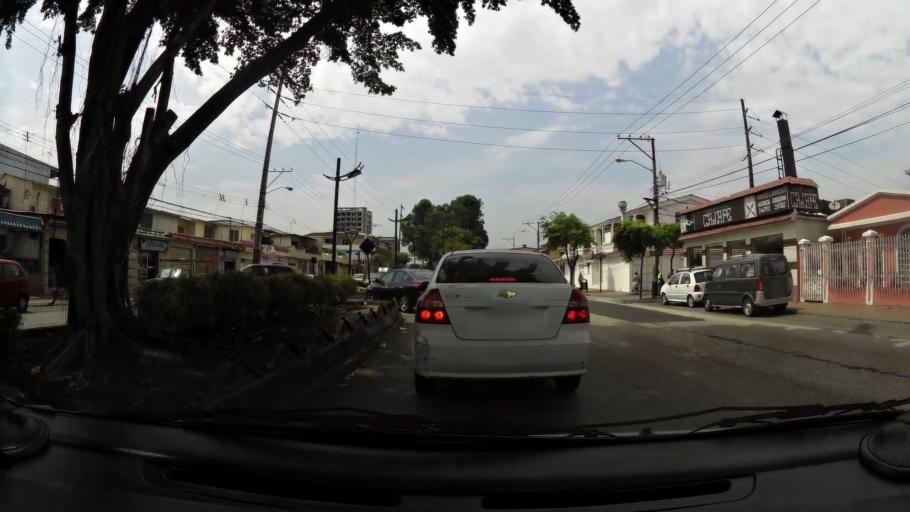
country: EC
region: Guayas
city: Eloy Alfaro
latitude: -2.1380
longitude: -79.9053
